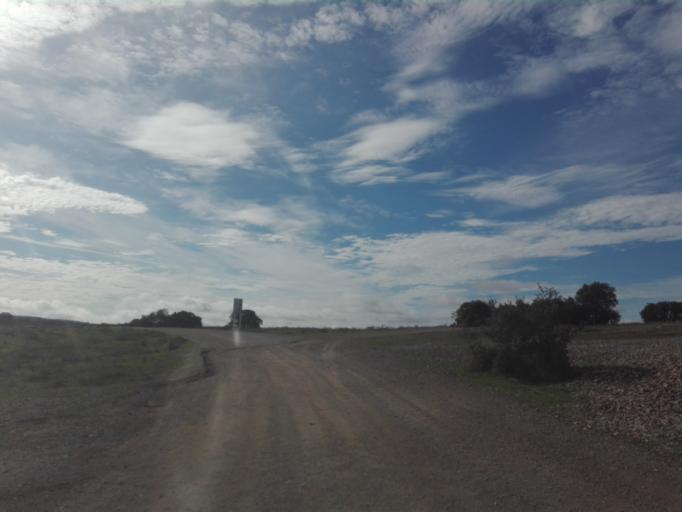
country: ES
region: Extremadura
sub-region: Provincia de Badajoz
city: Villagarcia de la Torre
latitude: 38.3024
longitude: -6.0924
